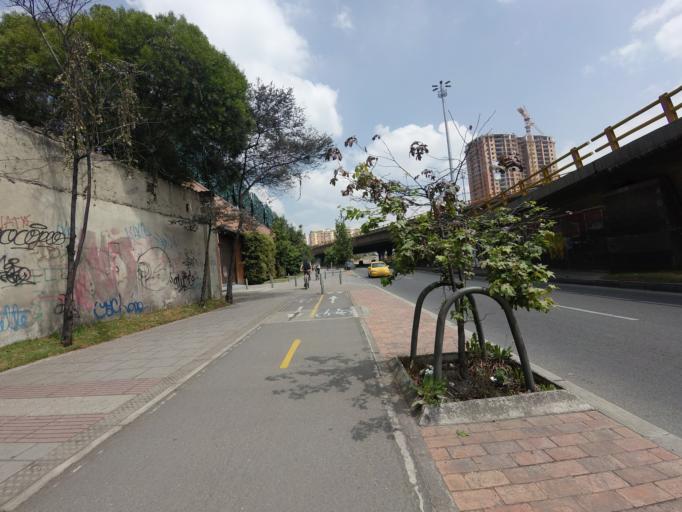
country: CO
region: Bogota D.C.
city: Barrio San Luis
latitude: 4.7211
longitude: -74.0751
